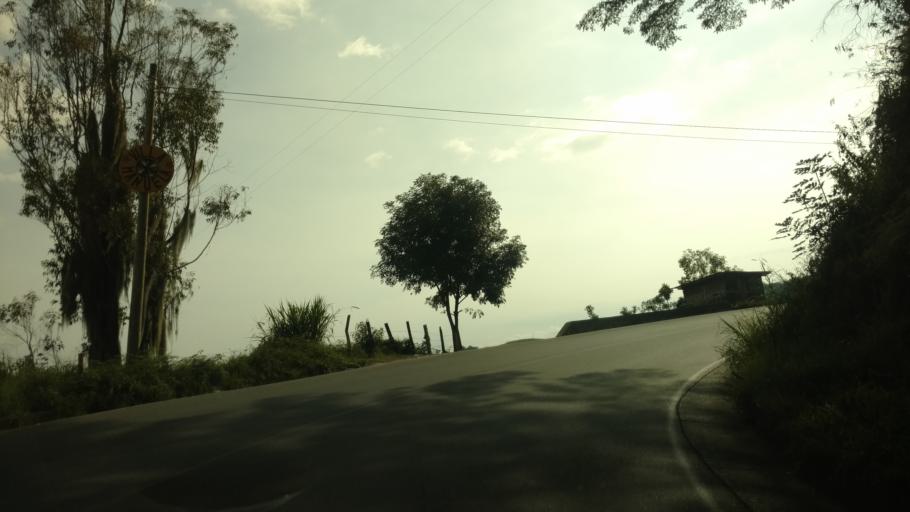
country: CO
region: Caldas
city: Neira
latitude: 5.1417
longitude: -75.5081
